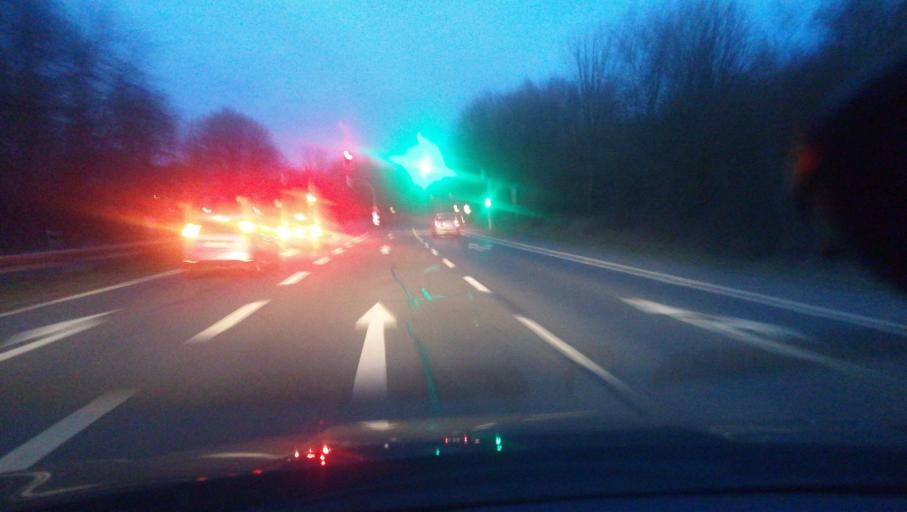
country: DE
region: North Rhine-Westphalia
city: Waltrop
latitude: 51.5564
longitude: 7.3992
